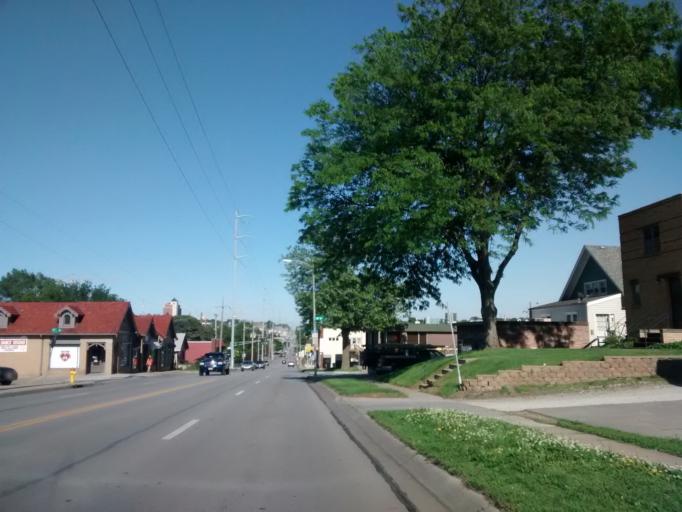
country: US
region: Nebraska
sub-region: Douglas County
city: Omaha
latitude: 41.2524
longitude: -95.9919
